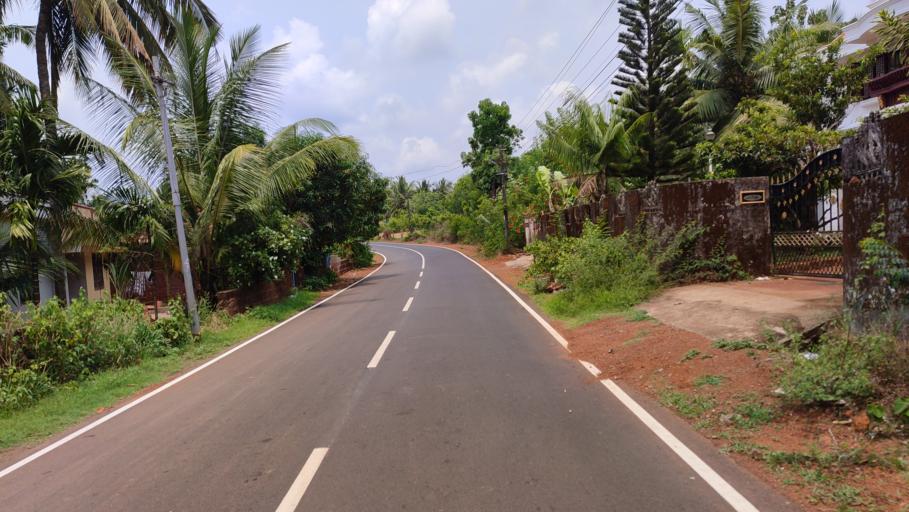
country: IN
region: Kerala
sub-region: Kasaragod District
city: Kannangad
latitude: 12.3184
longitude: 75.1179
